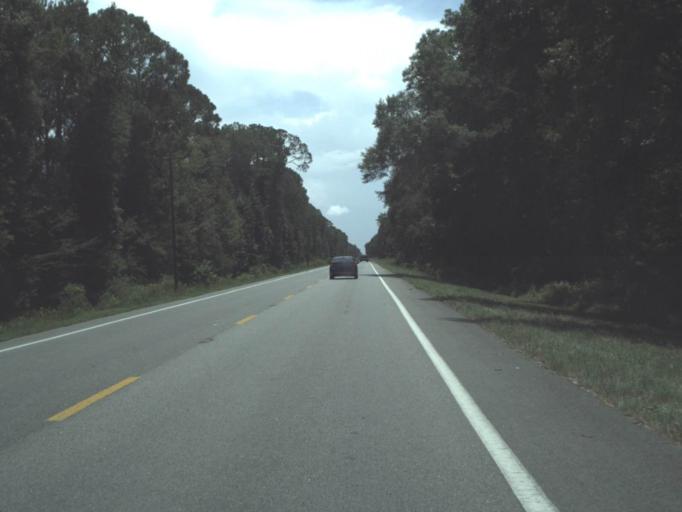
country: US
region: Florida
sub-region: Taylor County
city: Perry
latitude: 30.1211
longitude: -83.7337
